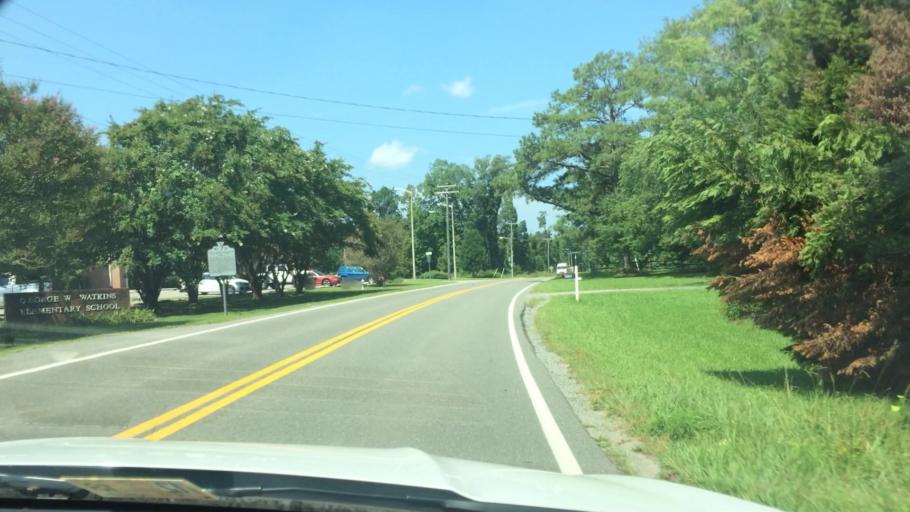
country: US
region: Virginia
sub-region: New Kent County
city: New Kent
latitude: 37.5298
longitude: -77.0979
